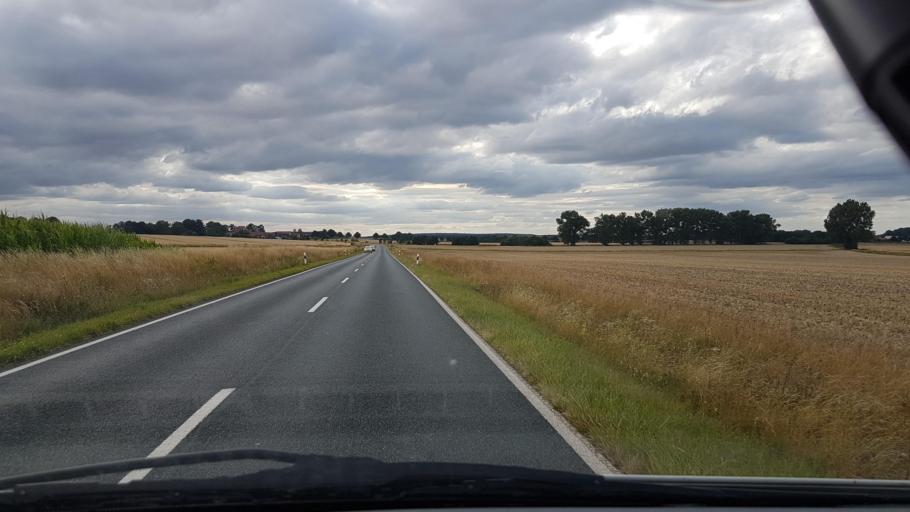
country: DE
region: Lower Saxony
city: Supplingenburg
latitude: 52.2515
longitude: 10.8814
